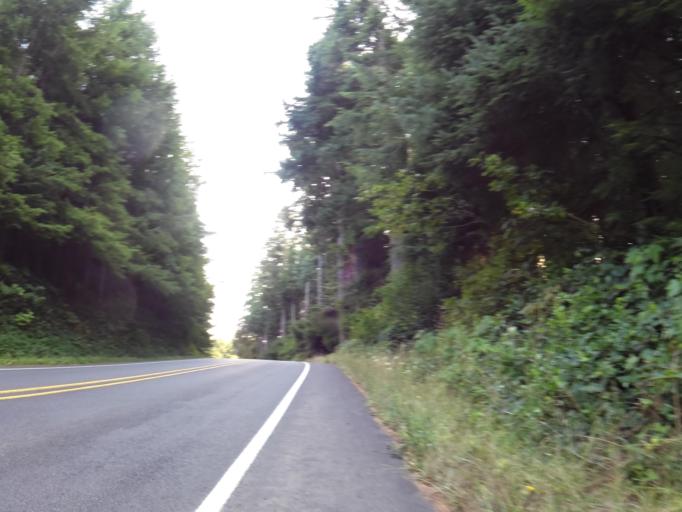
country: US
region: Oregon
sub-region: Lincoln County
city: Lincoln City
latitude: 44.9672
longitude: -123.9931
